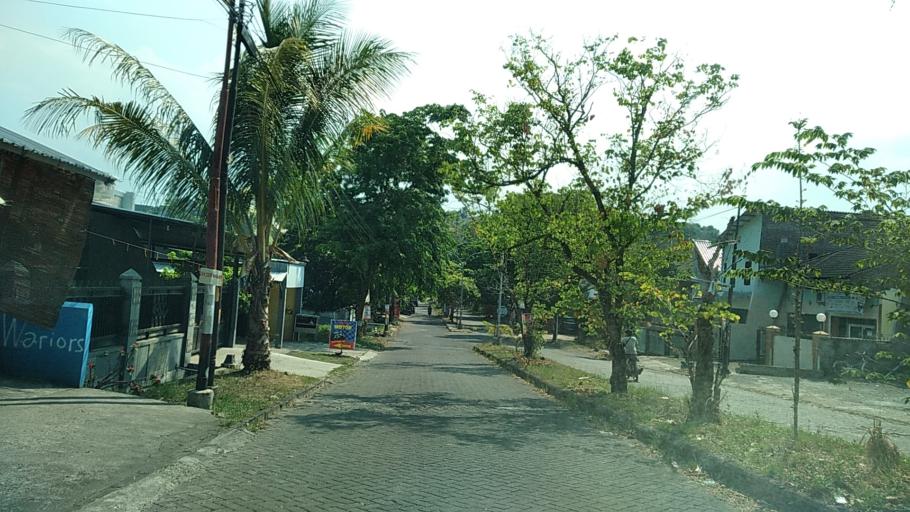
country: ID
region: Central Java
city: Mranggen
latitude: -7.0468
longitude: 110.4719
